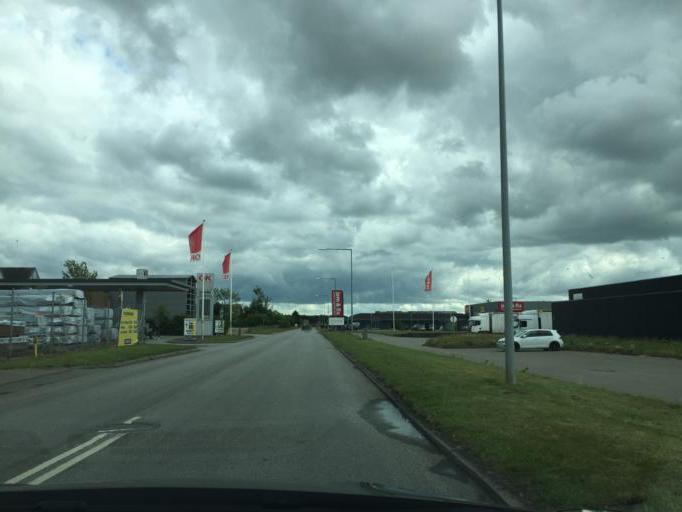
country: DK
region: South Denmark
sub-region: Haderslev Kommune
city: Vojens
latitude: 55.2423
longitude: 9.2709
